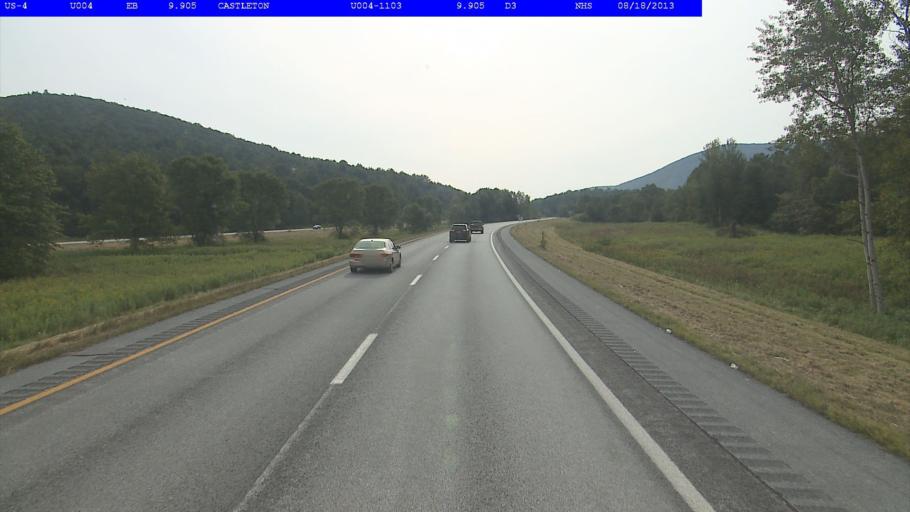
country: US
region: Vermont
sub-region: Rutland County
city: Castleton
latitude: 43.6164
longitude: -73.1244
